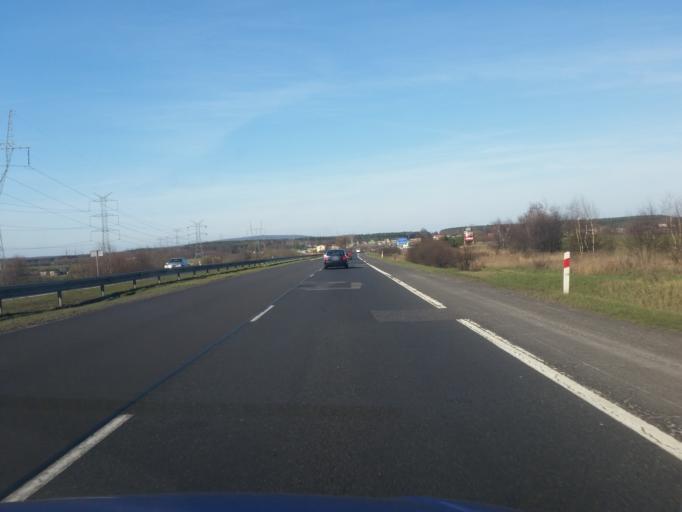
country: PL
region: Lodz Voivodeship
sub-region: Powiat radomszczanski
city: Radomsko
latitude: 51.0944
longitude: 19.3791
